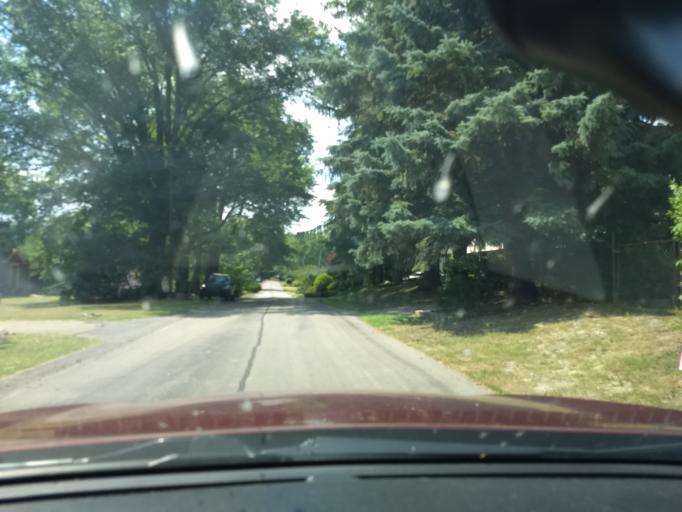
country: US
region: Pennsylvania
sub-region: Allegheny County
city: Monroeville
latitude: 40.4412
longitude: -79.7556
